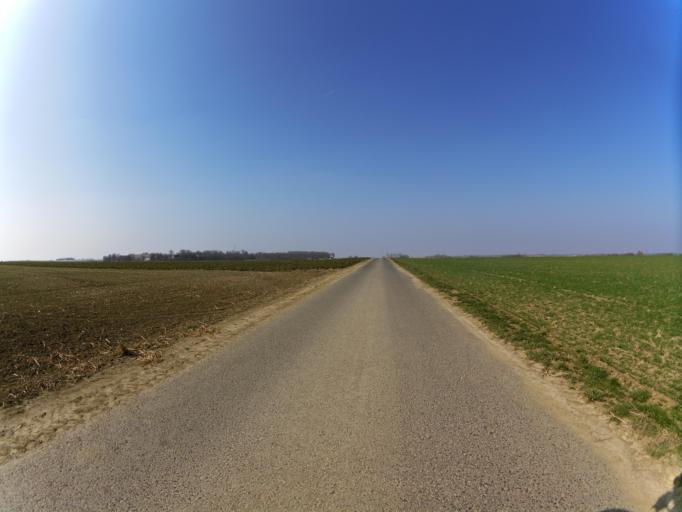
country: DE
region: Bavaria
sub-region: Regierungsbezirk Unterfranken
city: Gaukonigshofen
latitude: 49.6489
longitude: 9.9926
